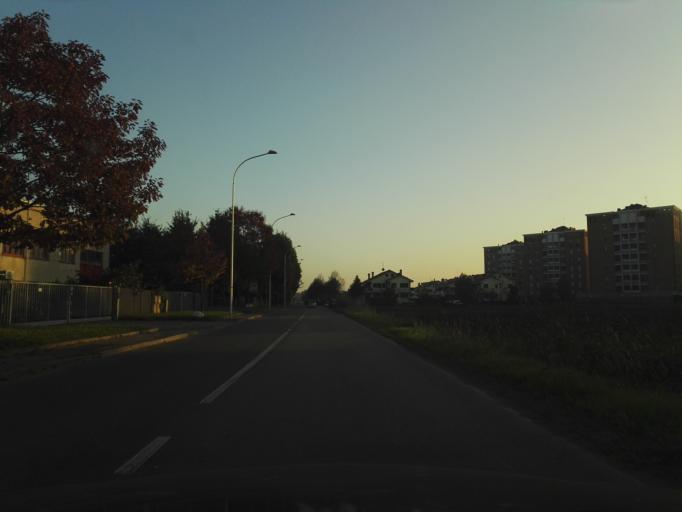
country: IT
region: Lombardy
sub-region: Citta metropolitana di Milano
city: Vigliano-Bettolino
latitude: 45.4364
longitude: 9.3466
